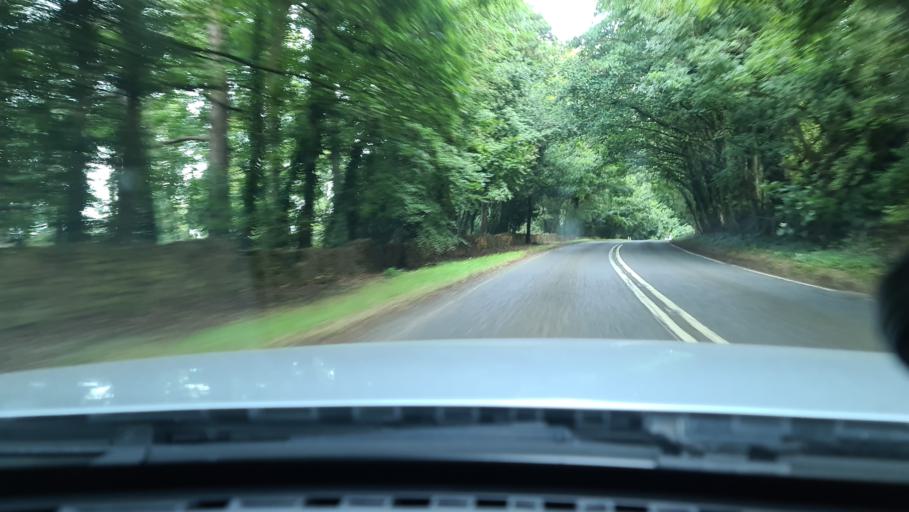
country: GB
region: England
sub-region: Oxfordshire
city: Hanwell
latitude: 52.1054
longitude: -1.4526
